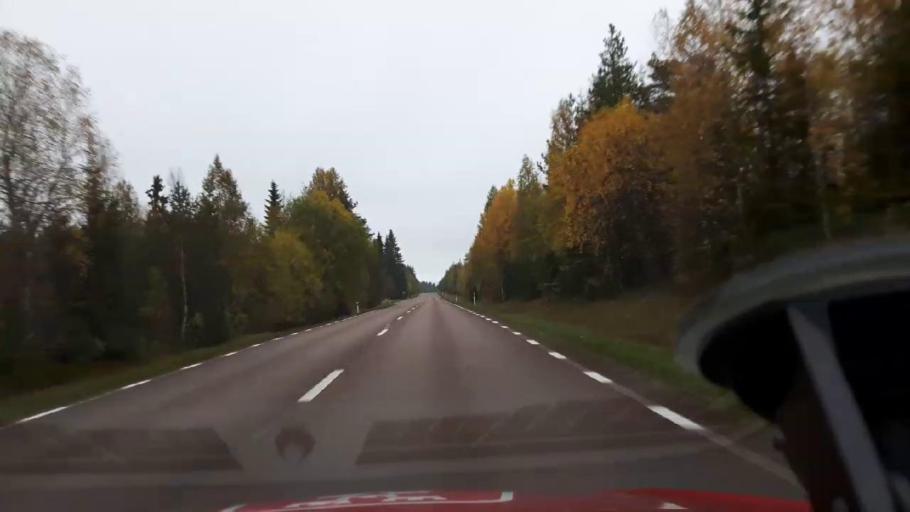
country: SE
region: Jaemtland
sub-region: Bergs Kommun
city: Hoverberg
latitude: 62.5842
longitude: 14.4392
